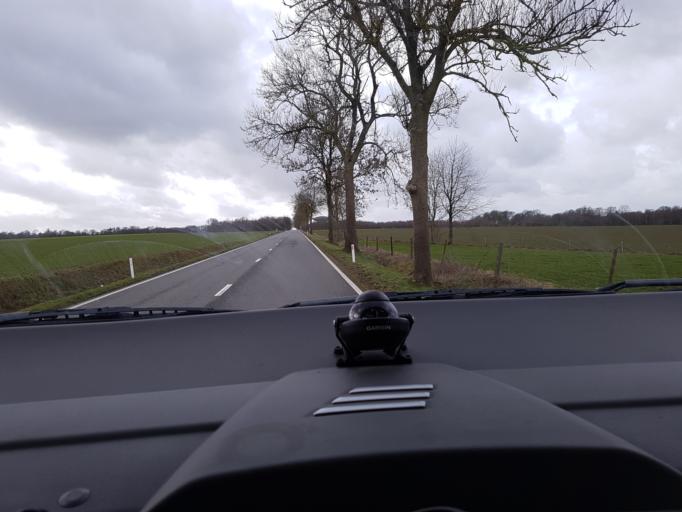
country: BE
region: Wallonia
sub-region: Province de Namur
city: Florennes
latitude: 50.2280
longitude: 4.6652
